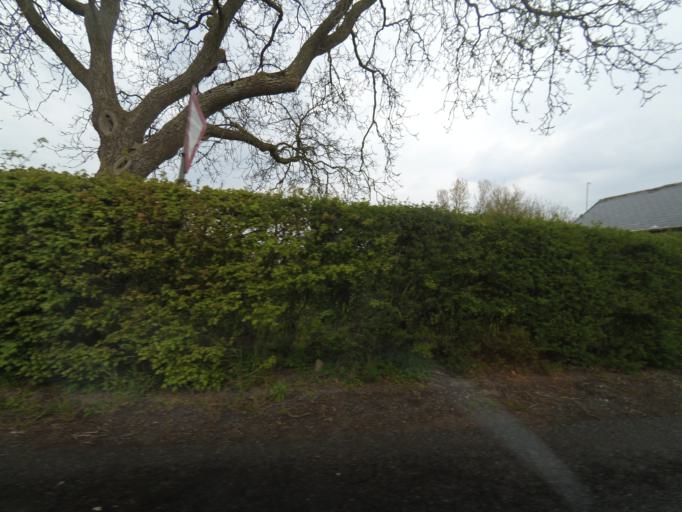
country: DK
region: South Denmark
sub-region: Faaborg-Midtfyn Kommune
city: Ringe
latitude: 55.1923
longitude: 10.5453
